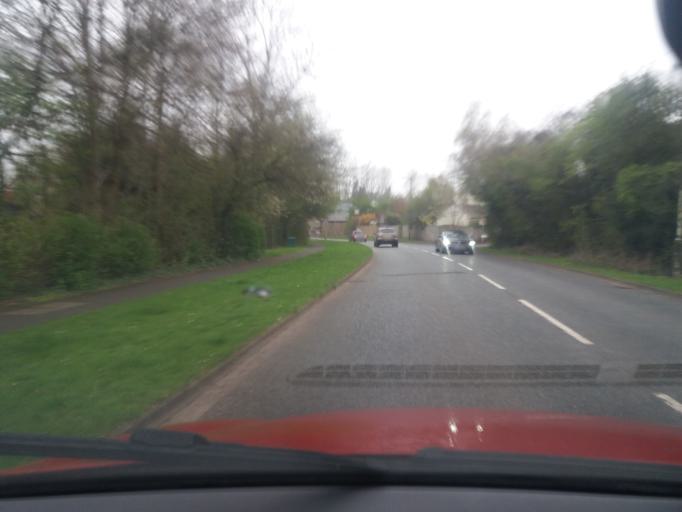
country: GB
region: England
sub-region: Lancashire
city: Clayton-le-Woods
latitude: 53.7028
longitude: -2.6352
